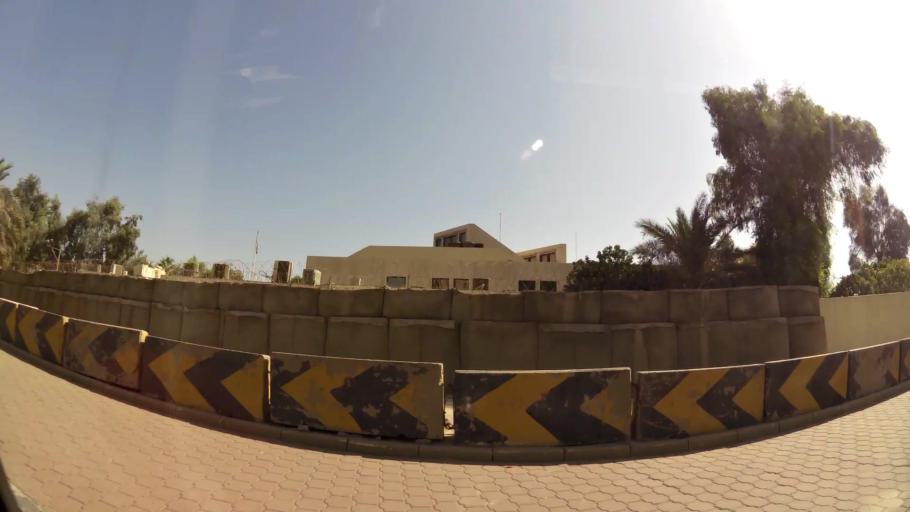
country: KW
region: Al Asimah
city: Kuwait City
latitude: 29.3899
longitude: 47.9941
